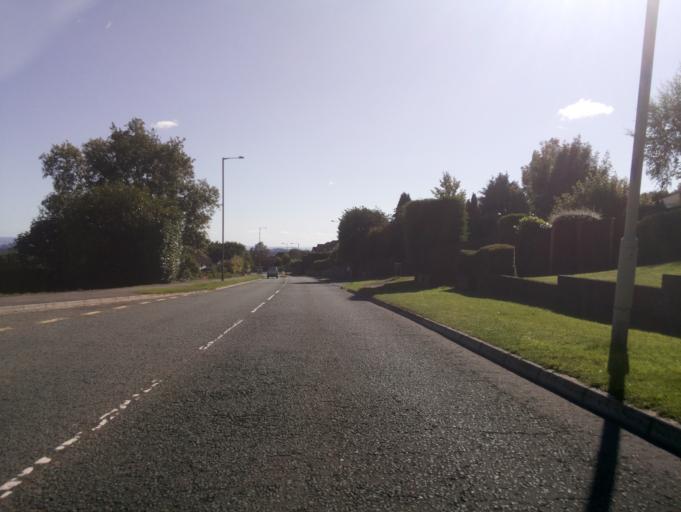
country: GB
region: Wales
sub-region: Torfaen County Borough
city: Cwmbran
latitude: 51.6477
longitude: -3.0606
